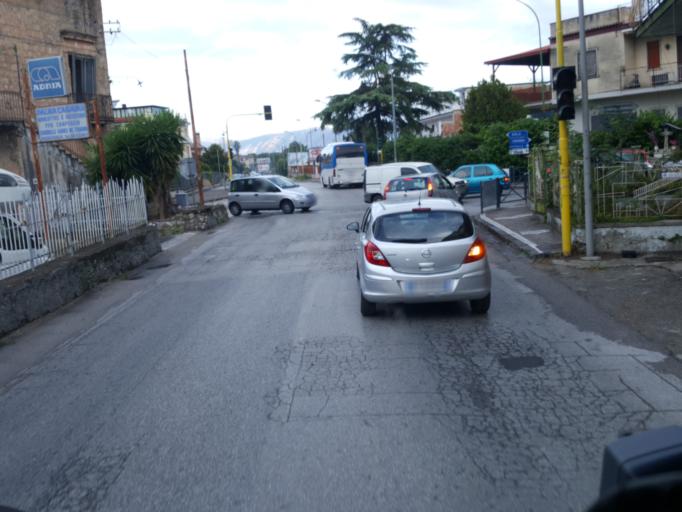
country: IT
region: Campania
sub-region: Provincia di Napoli
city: Palma Campania
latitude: 40.8797
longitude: 14.5506
